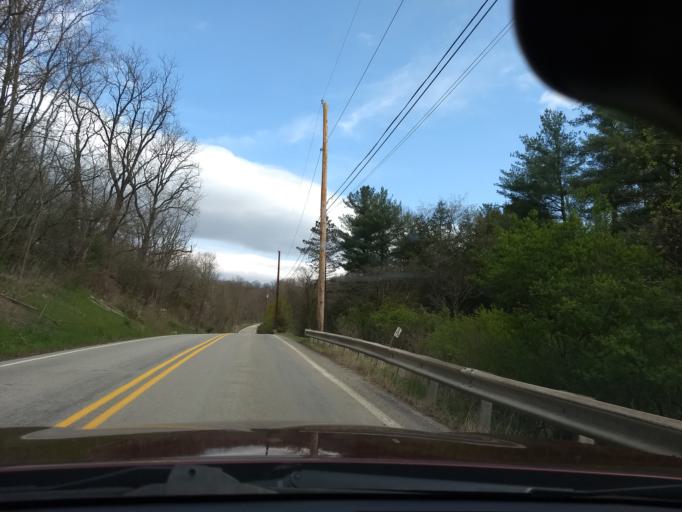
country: US
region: Pennsylvania
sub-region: Allegheny County
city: Allison Park
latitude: 40.5488
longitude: -79.9123
